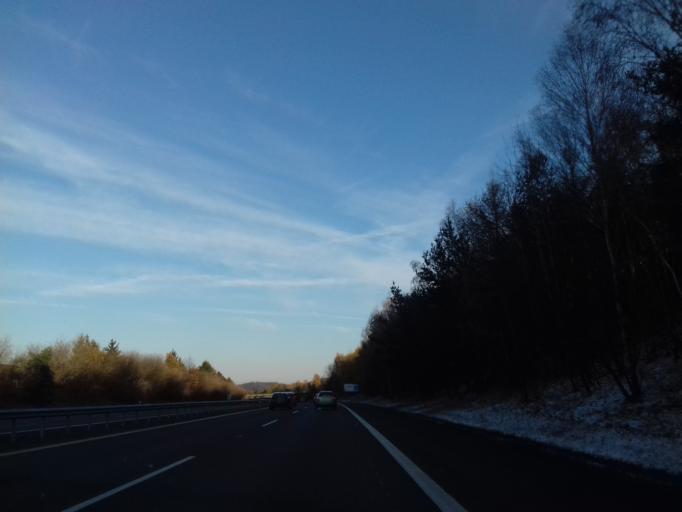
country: CZ
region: Central Bohemia
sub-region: Okres Beroun
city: Lodenice
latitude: 49.9796
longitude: 14.1243
